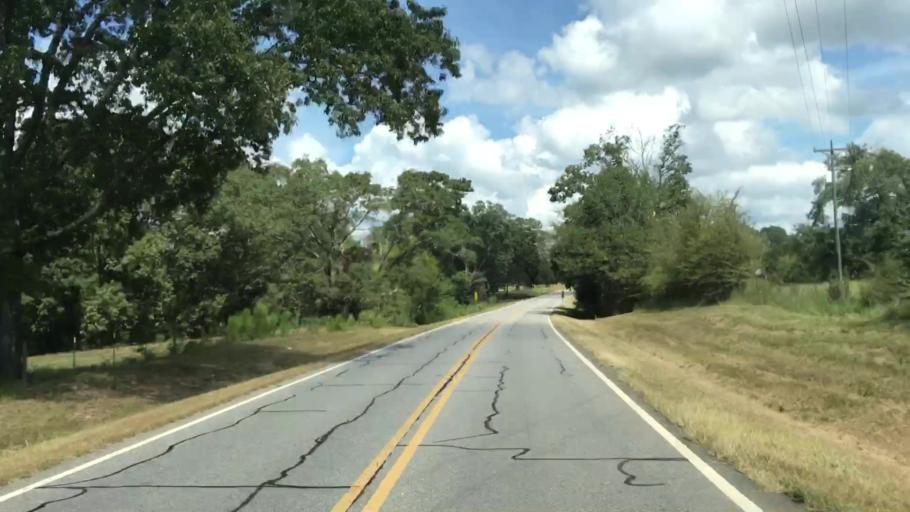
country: US
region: Georgia
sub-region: Oconee County
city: Watkinsville
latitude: 33.7401
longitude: -83.3033
